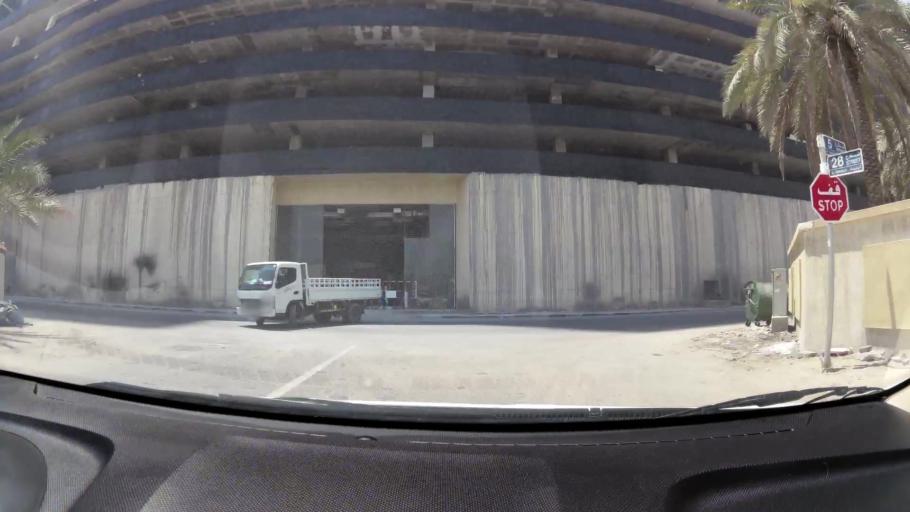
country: AE
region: Ajman
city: Ajman
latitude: 25.4043
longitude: 55.4308
